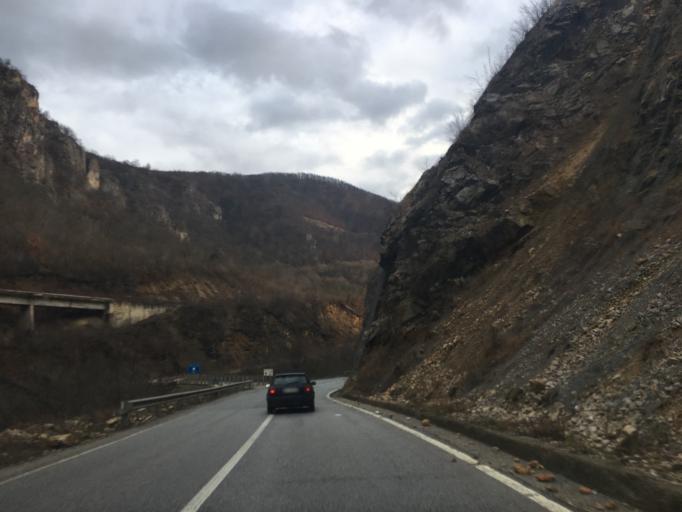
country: RS
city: Sokolovo Brdo
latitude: 43.1583
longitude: 19.7776
